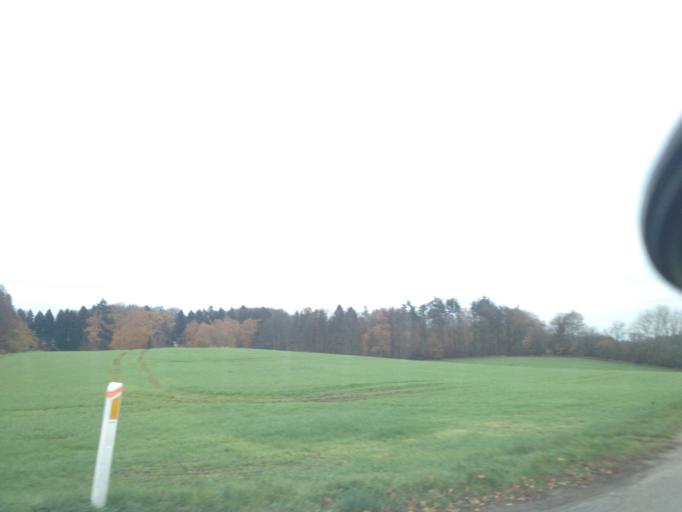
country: DK
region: South Denmark
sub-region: Assens Kommune
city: Vissenbjerg
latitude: 55.4223
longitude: 10.1653
